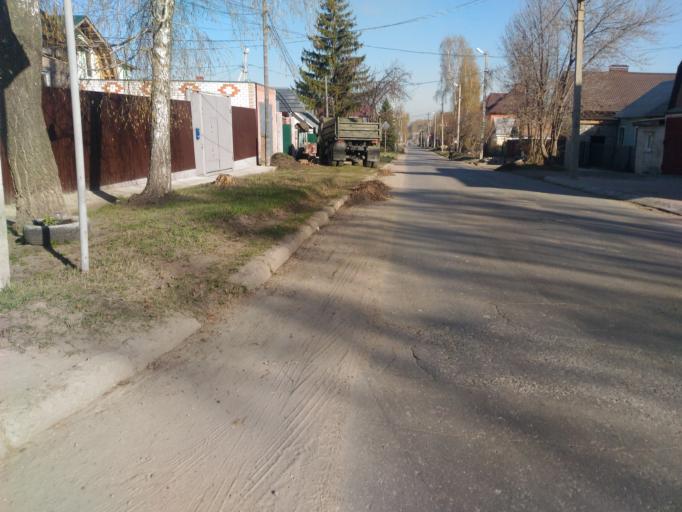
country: RU
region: Ulyanovsk
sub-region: Ulyanovskiy Rayon
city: Ulyanovsk
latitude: 54.3500
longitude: 48.3771
